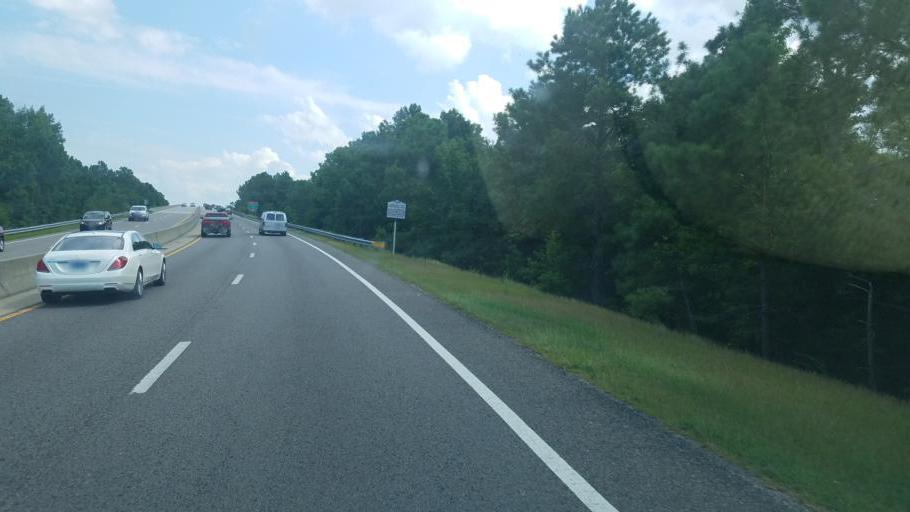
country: US
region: North Carolina
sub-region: Currituck County
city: Currituck
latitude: 36.3447
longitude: -75.9589
